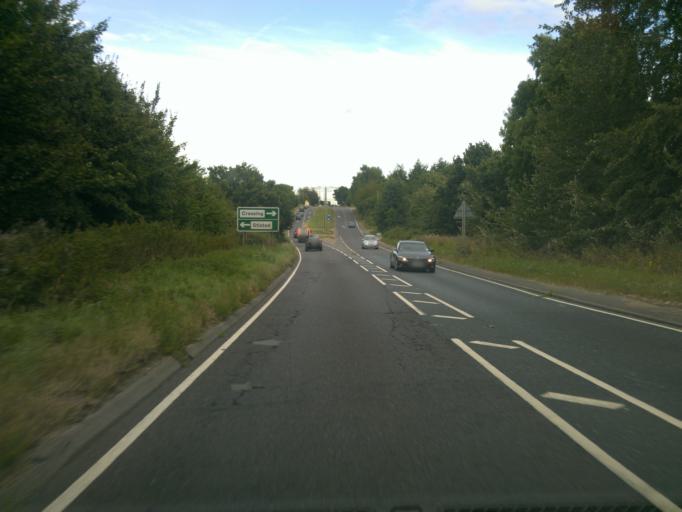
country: GB
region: England
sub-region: Essex
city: Rayne
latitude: 51.8795
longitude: 0.6090
